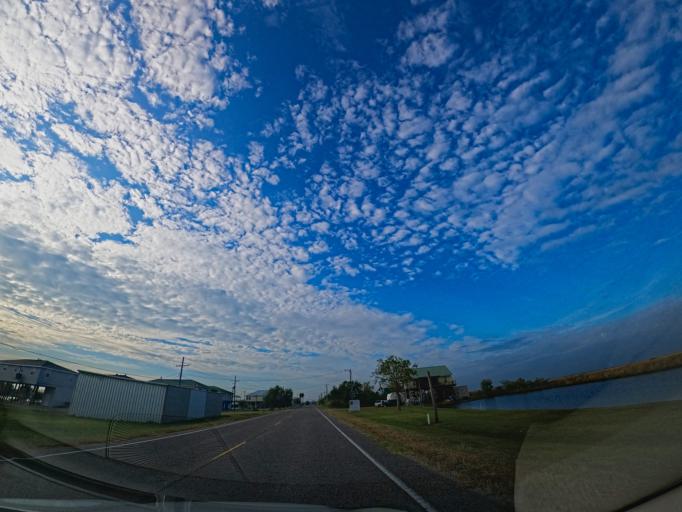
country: US
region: Louisiana
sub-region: Terrebonne Parish
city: Dulac
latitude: 29.3035
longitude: -90.6484
